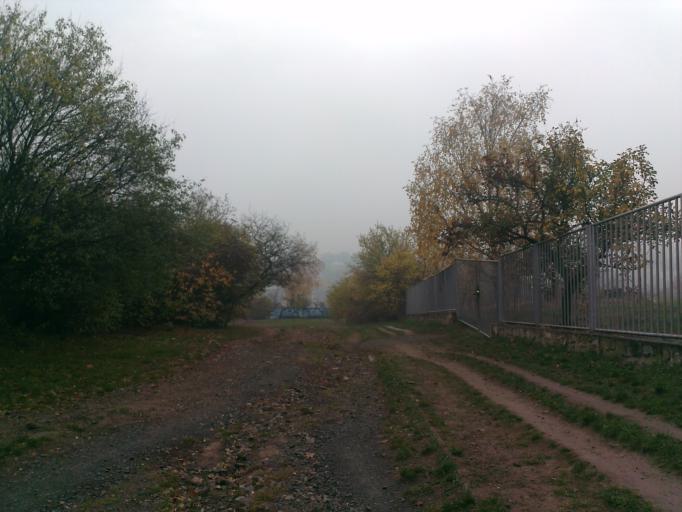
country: CZ
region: South Moravian
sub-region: Mesto Brno
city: Brno
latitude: 49.2008
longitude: 16.5889
